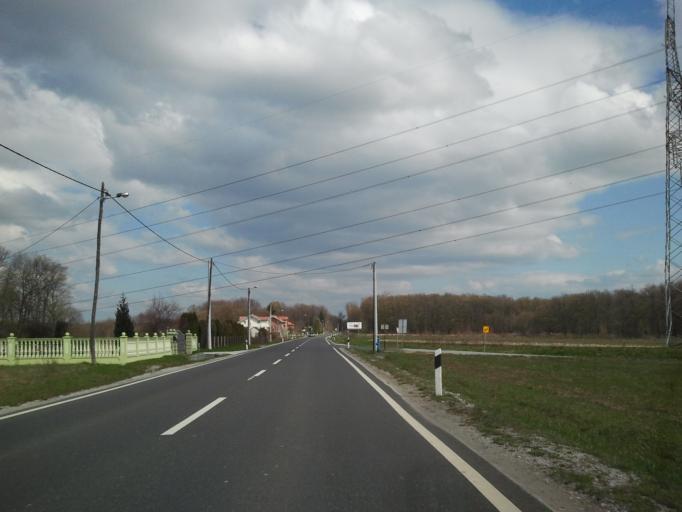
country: HR
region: Grad Zagreb
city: Horvati
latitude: 45.7145
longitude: 15.7788
